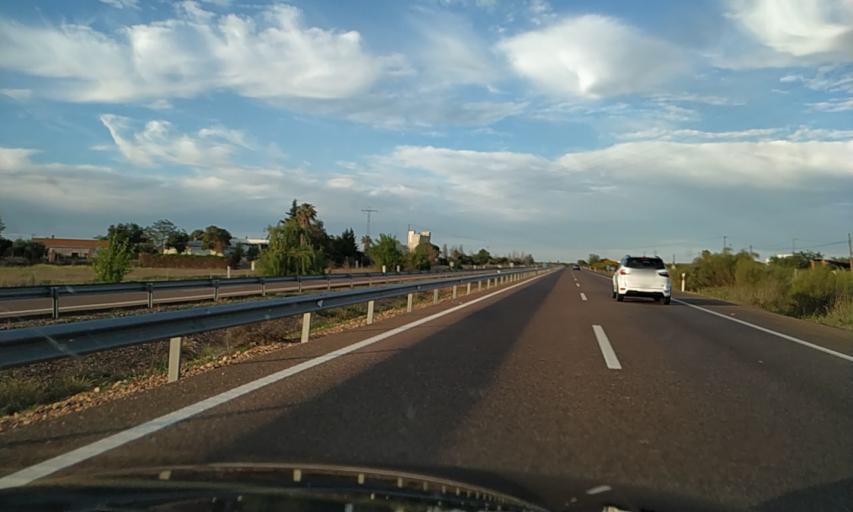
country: ES
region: Extremadura
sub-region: Provincia de Badajoz
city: Calamonte
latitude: 38.8909
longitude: -6.4249
